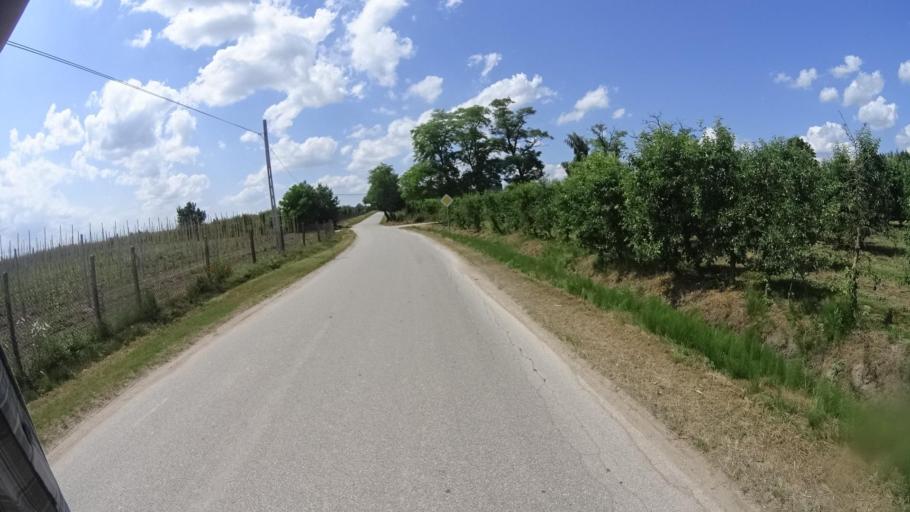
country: PL
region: Masovian Voivodeship
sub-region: Powiat grojecki
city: Goszczyn
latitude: 51.7259
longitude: 20.8454
